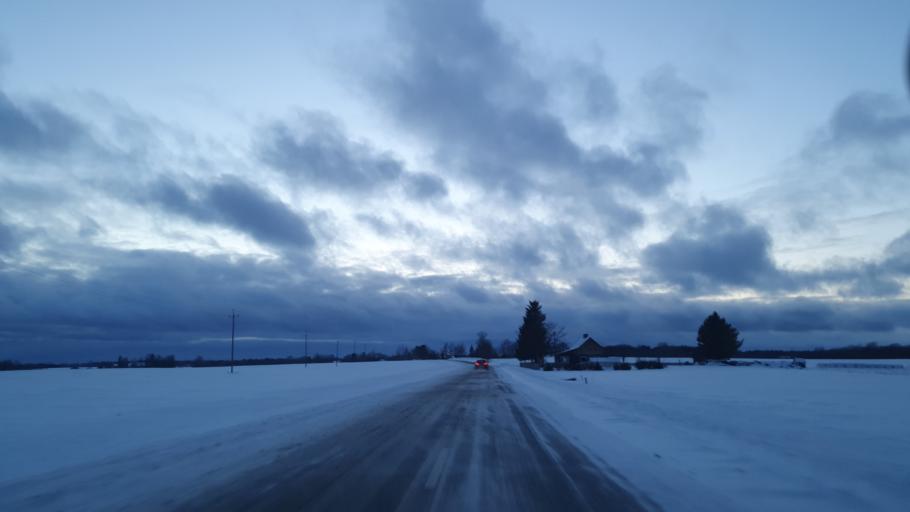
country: EE
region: Jogevamaa
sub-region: Jogeva linn
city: Jogeva
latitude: 58.6131
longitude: 26.4028
